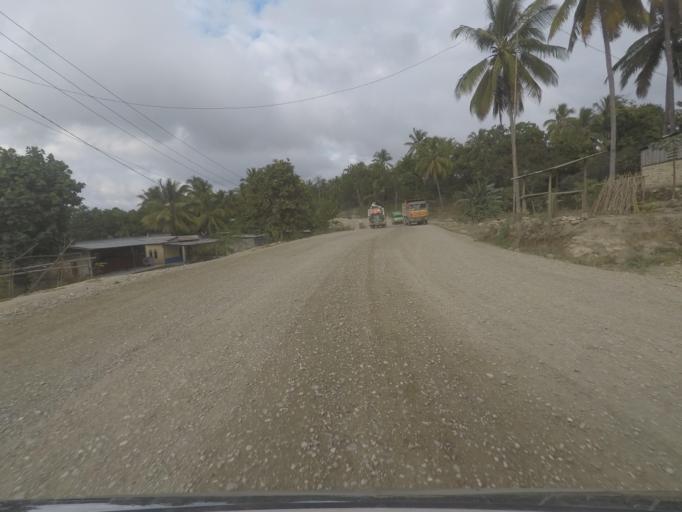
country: TL
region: Baucau
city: Baucau
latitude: -8.5135
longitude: 126.4410
